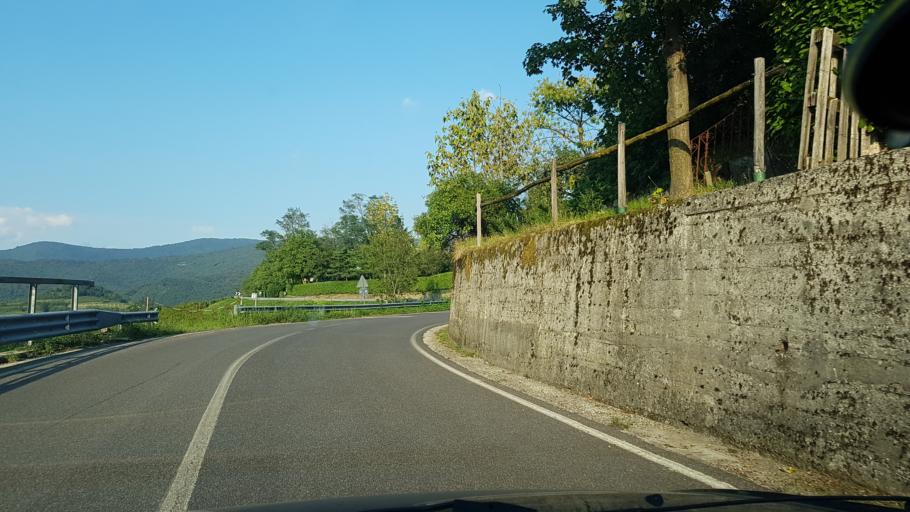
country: IT
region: Friuli Venezia Giulia
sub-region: Provincia di Gorizia
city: San Floriano del Collio
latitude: 45.9849
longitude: 13.5886
